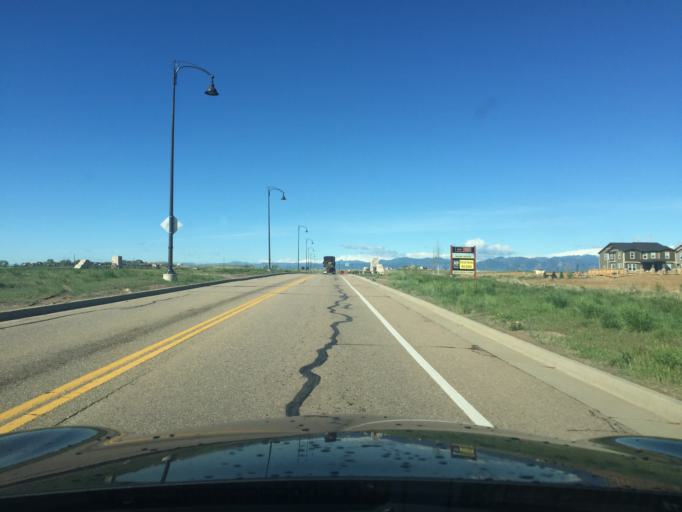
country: US
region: Colorado
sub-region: Boulder County
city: Erie
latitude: 39.9943
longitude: -105.0112
